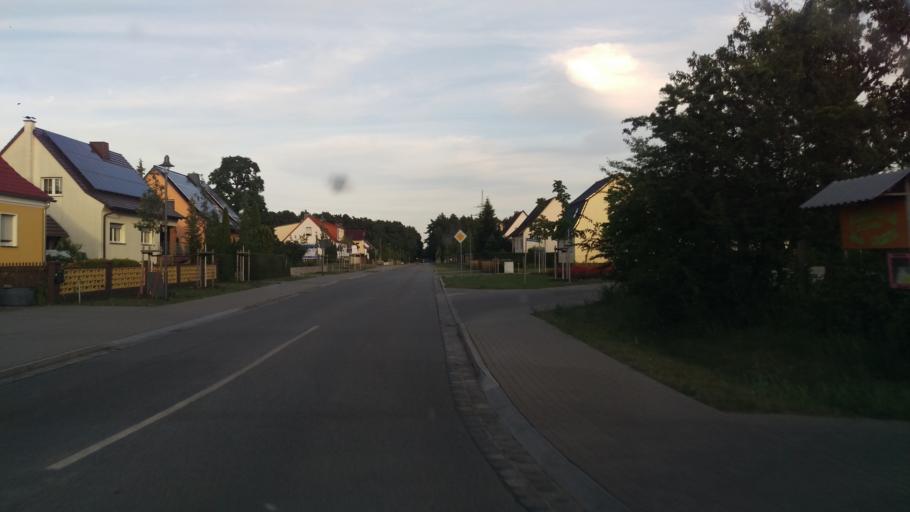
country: DE
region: Brandenburg
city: Ziltendorf
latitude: 52.2027
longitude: 14.6294
